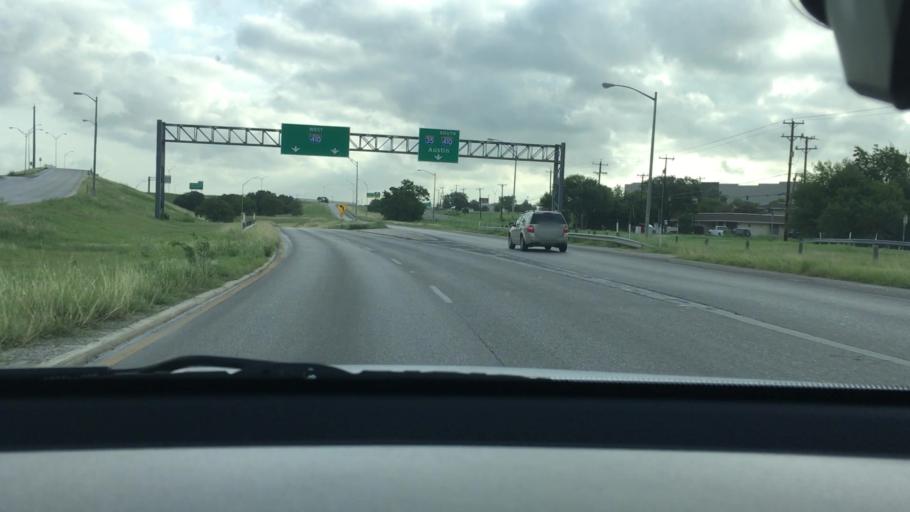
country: US
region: Texas
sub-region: Bexar County
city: Windcrest
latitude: 29.5134
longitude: -98.4038
